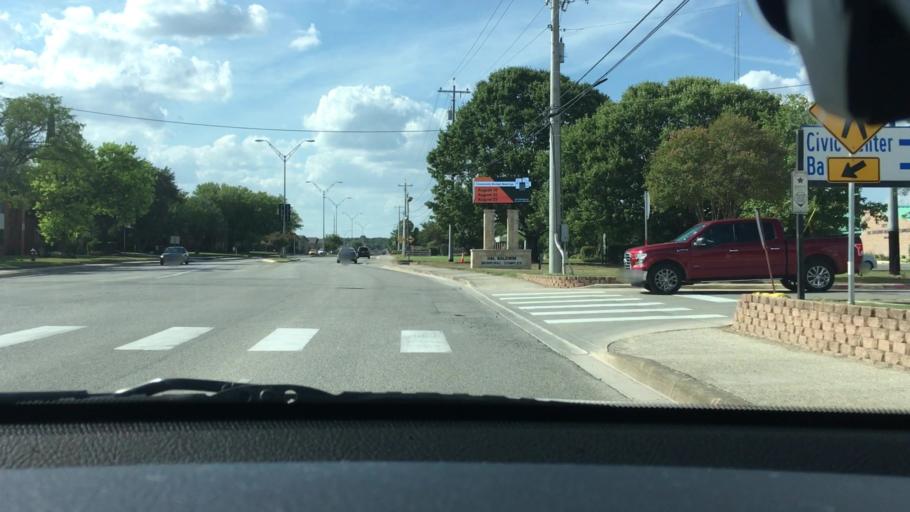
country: US
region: Texas
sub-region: Guadalupe County
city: Schertz
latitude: 29.5641
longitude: -98.2694
